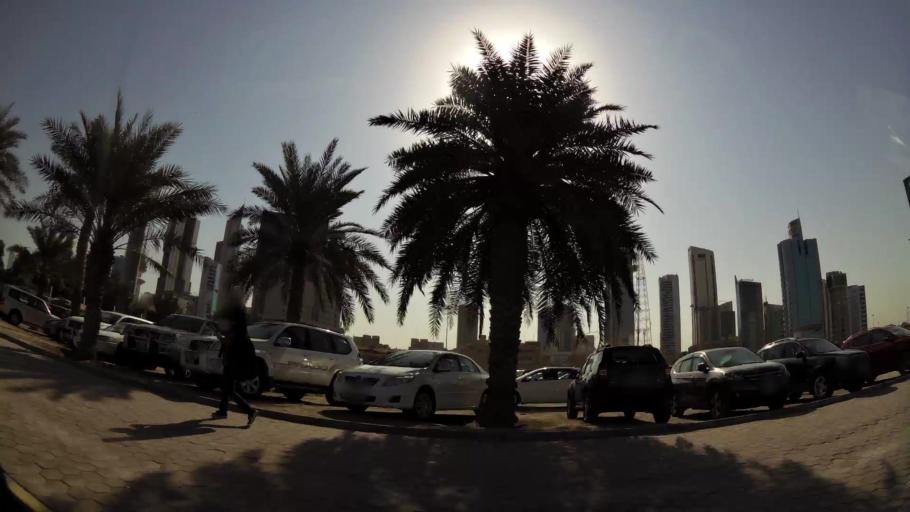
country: KW
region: Al Asimah
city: Kuwait City
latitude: 29.3671
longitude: 47.9606
